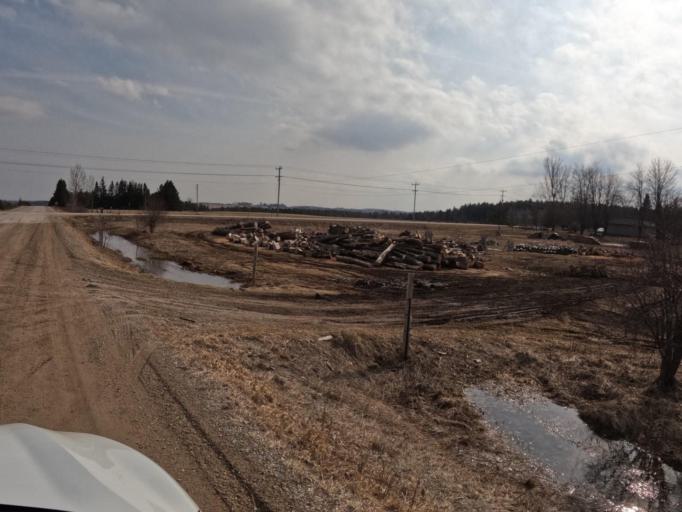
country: CA
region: Ontario
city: Orangeville
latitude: 43.9086
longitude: -80.2868
